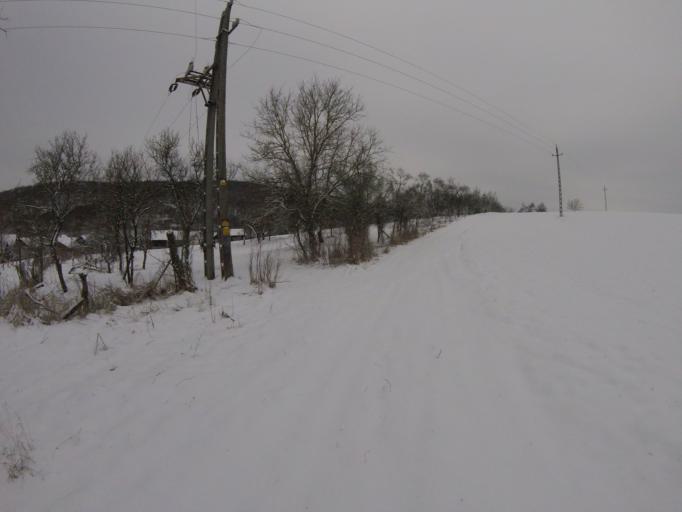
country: HU
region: Borsod-Abauj-Zemplen
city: Rudabanya
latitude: 48.4447
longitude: 20.6252
